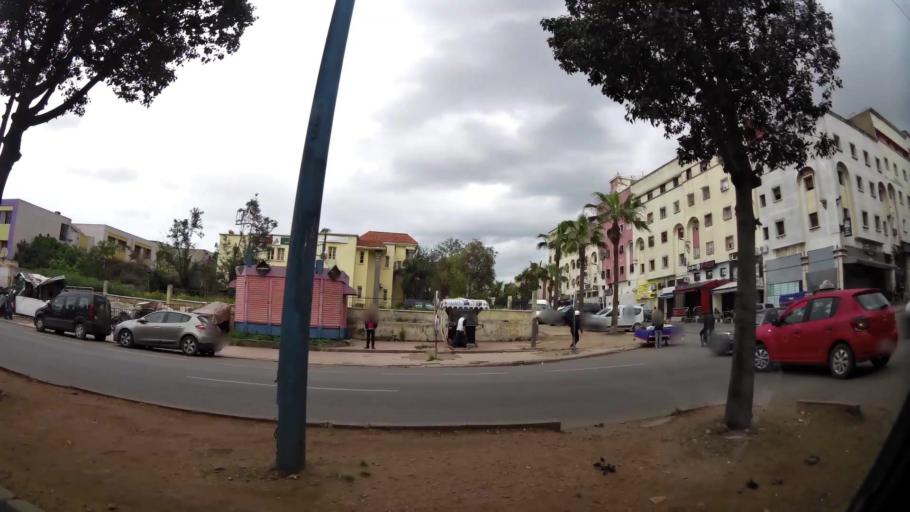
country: MA
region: Grand Casablanca
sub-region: Casablanca
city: Casablanca
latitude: 33.5619
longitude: -7.5528
